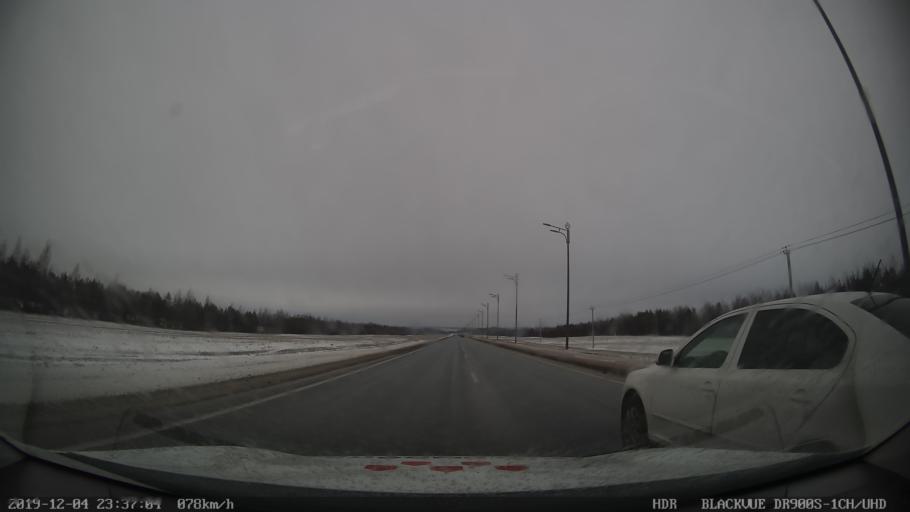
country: RU
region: Tatarstan
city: Stolbishchi
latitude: 55.6246
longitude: 49.2943
